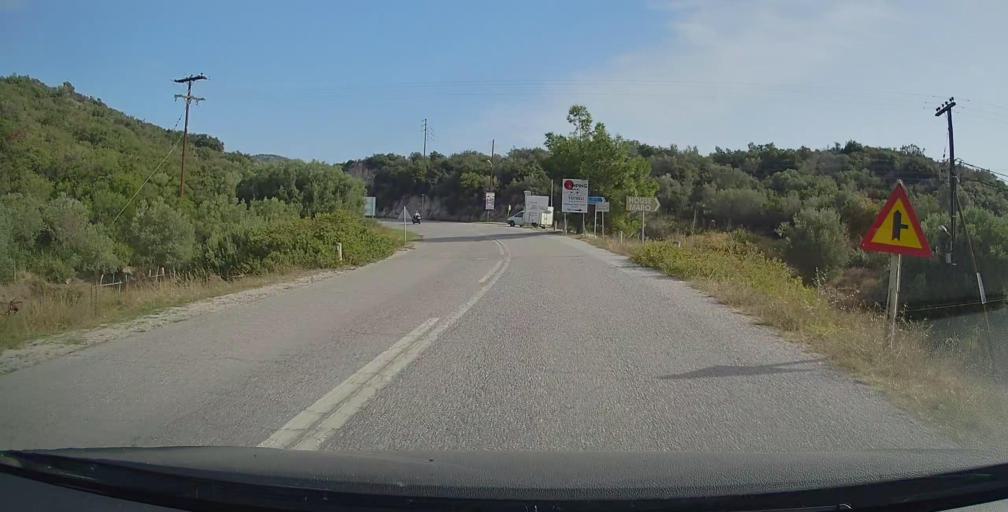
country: GR
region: Central Macedonia
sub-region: Nomos Chalkidikis
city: Sykia
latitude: 39.9922
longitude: 23.9893
